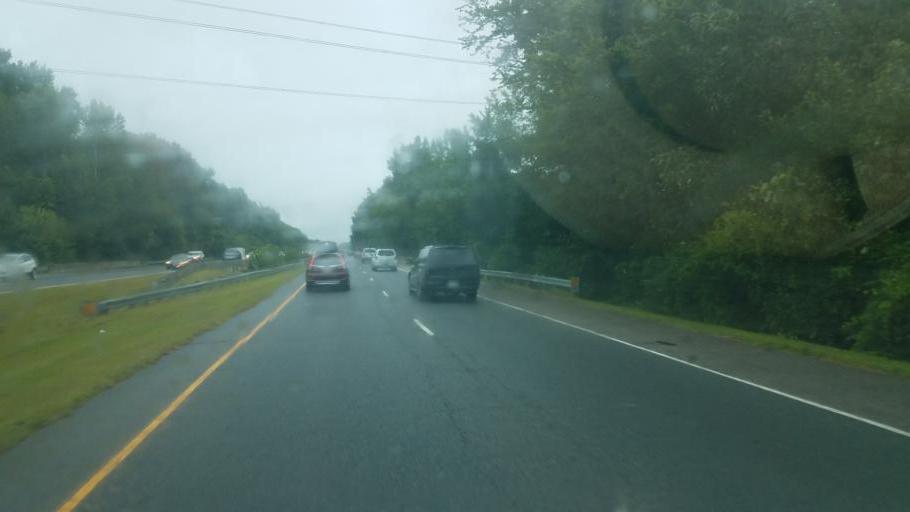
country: US
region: Virginia
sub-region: City of Chesapeake
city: Chesapeake
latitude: 36.6975
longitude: -76.2271
